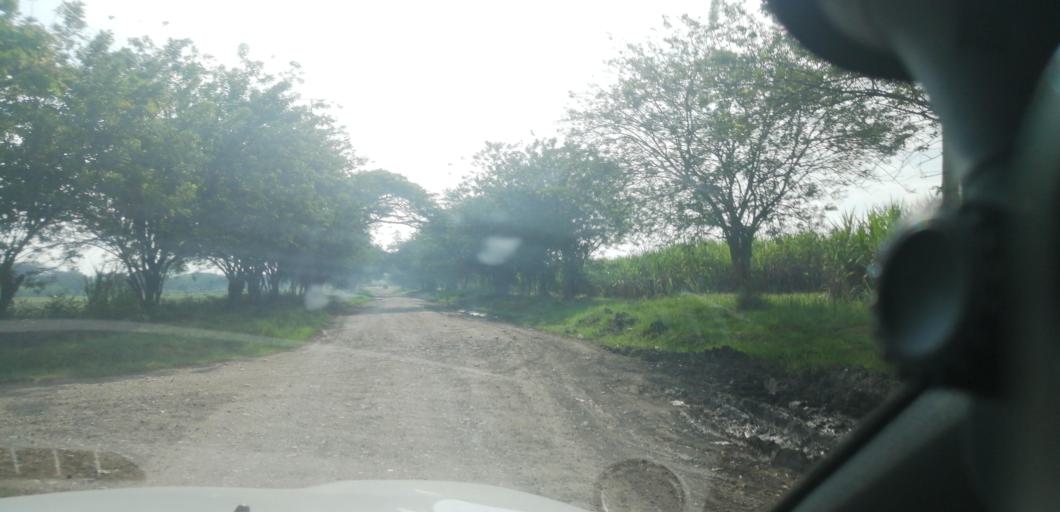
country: CO
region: Valle del Cauca
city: Yumbo
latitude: 3.5769
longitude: -76.4107
